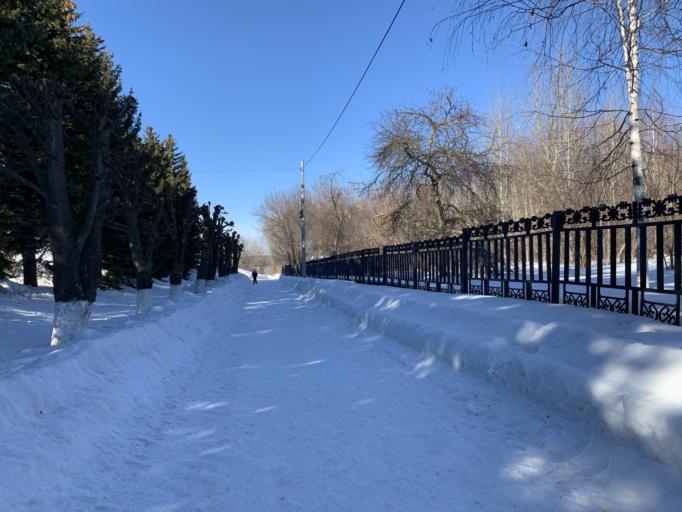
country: RU
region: Chuvashia
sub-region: Cheboksarskiy Rayon
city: Cheboksary
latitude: 56.1479
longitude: 47.2700
